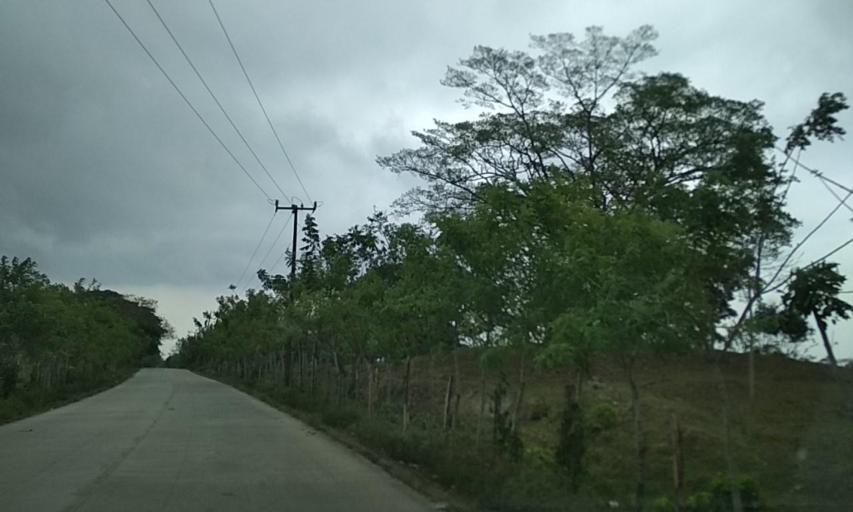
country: MX
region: Tabasco
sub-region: Huimanguillo
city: Francisco Rueda
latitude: 17.6470
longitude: -94.0932
